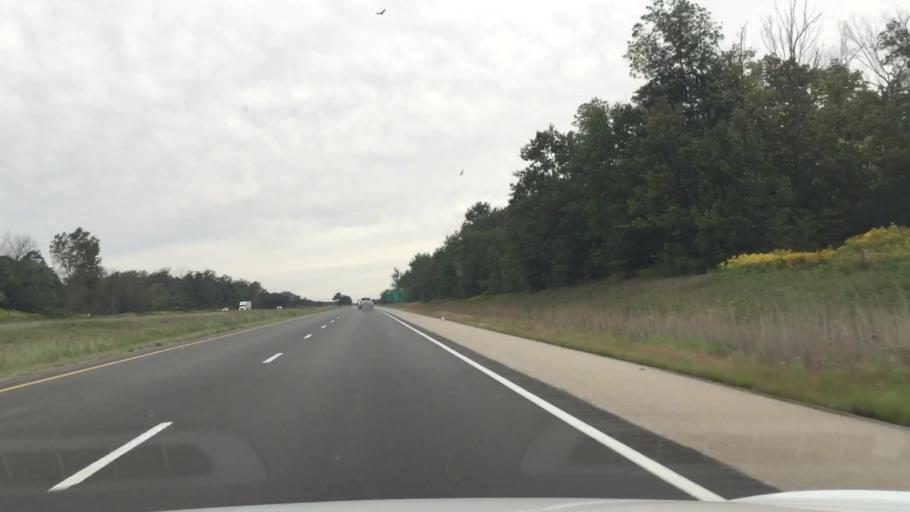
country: CA
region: Ontario
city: Lambton Shores
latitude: 42.9923
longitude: -81.8584
